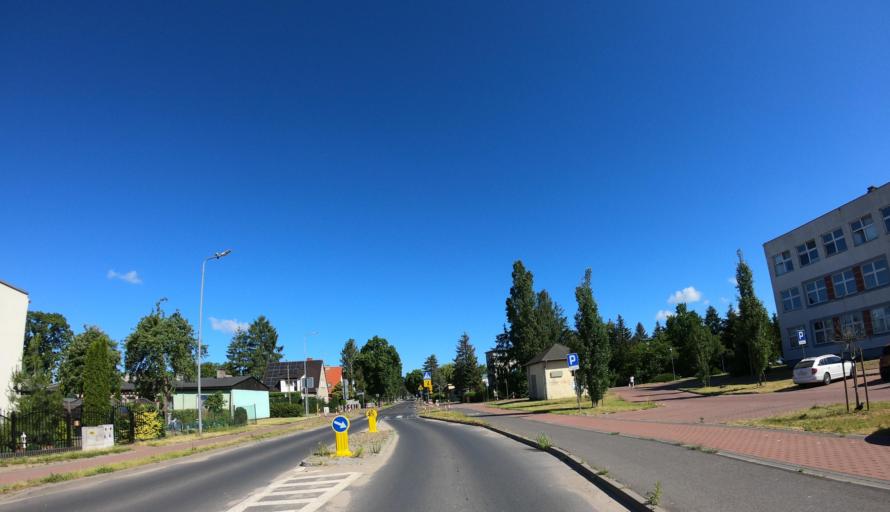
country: PL
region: West Pomeranian Voivodeship
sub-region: Powiat kamienski
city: Kamien Pomorski
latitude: 53.9609
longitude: 14.7758
